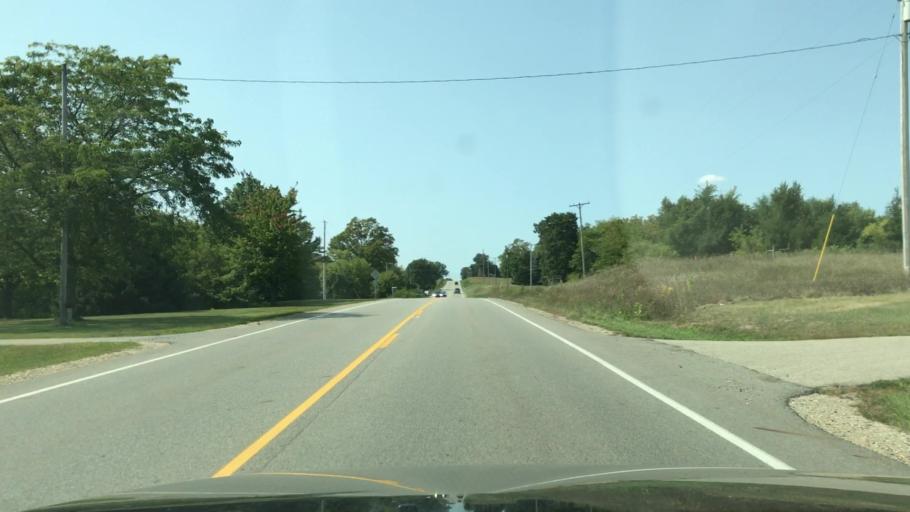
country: US
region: Michigan
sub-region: Kent County
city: Byron Center
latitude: 42.8118
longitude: -85.7866
